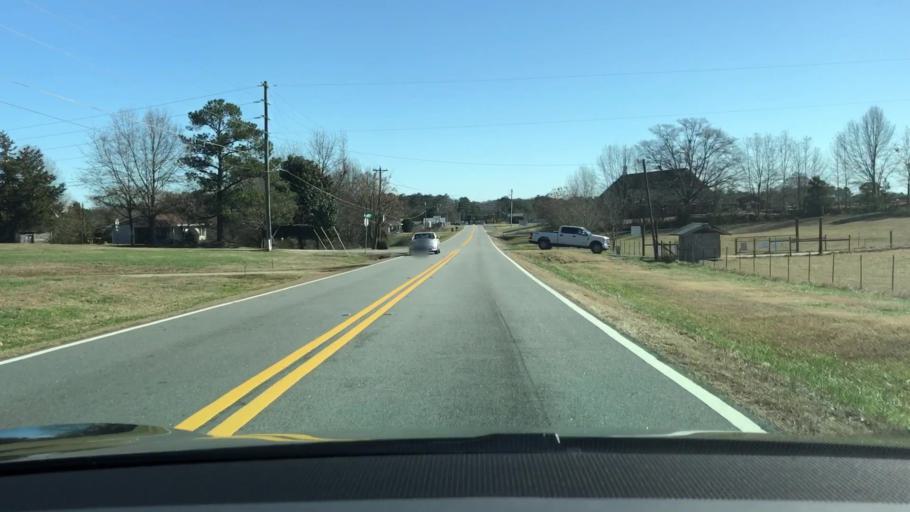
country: US
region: Georgia
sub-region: Barrow County
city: Auburn
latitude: 33.9029
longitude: -83.8079
